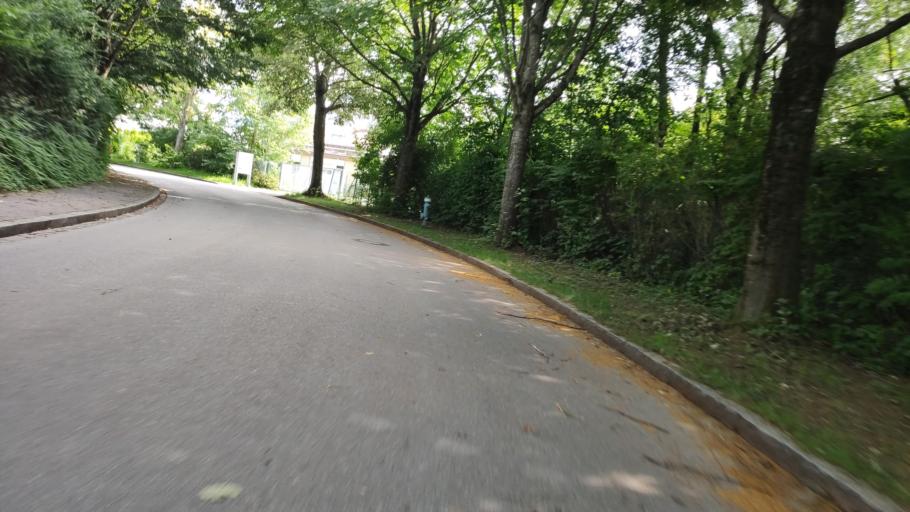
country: DE
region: Bavaria
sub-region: Swabia
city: Bobingen
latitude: 48.2707
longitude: 10.8423
